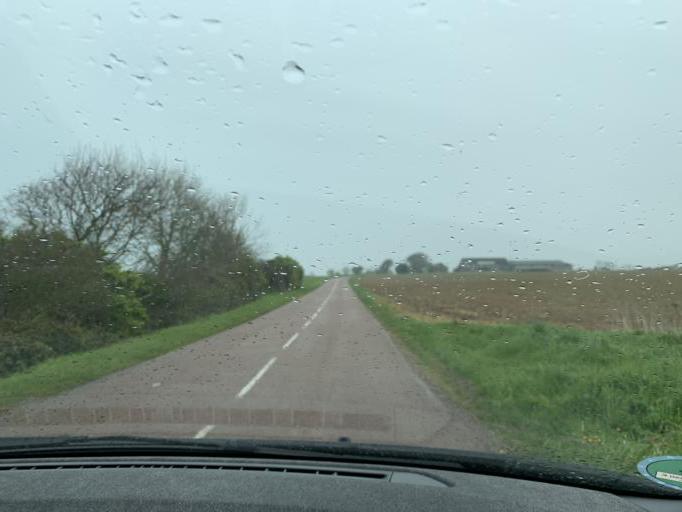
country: FR
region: Haute-Normandie
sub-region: Departement de la Seine-Maritime
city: Yport
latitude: 49.7358
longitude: 0.2995
